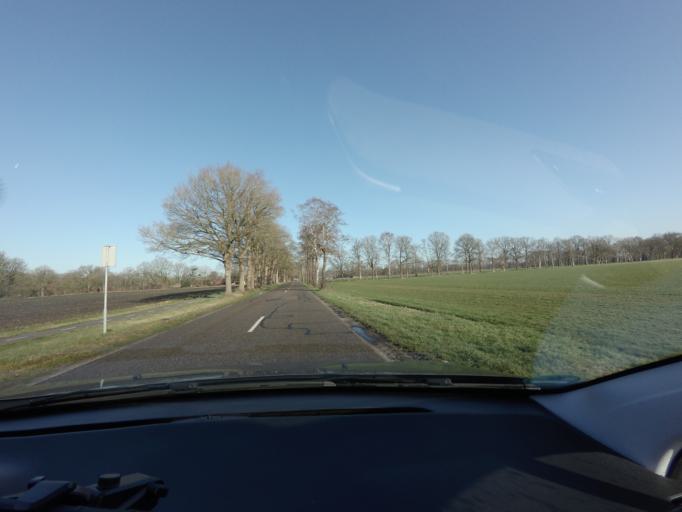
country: NL
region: Drenthe
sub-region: Gemeente Assen
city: Assen
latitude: 52.8625
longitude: 6.5881
